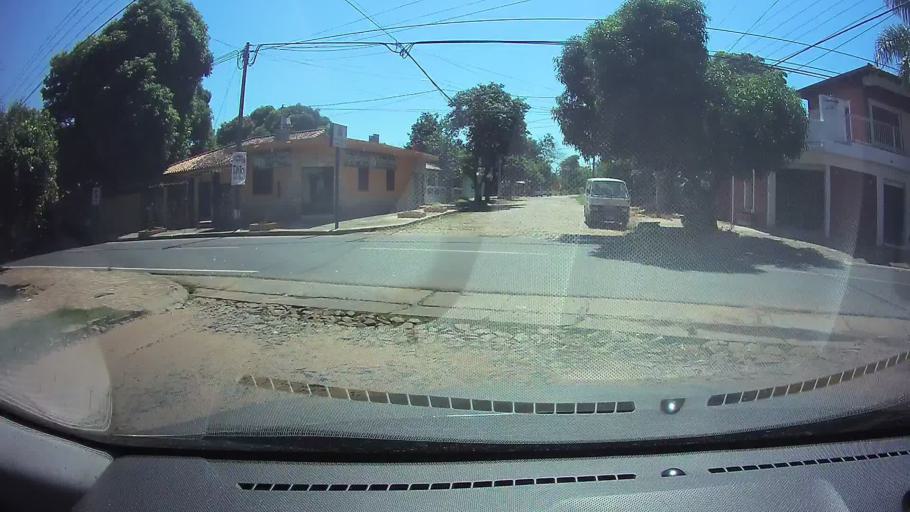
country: PY
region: Central
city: Fernando de la Mora
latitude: -25.3029
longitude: -57.5283
